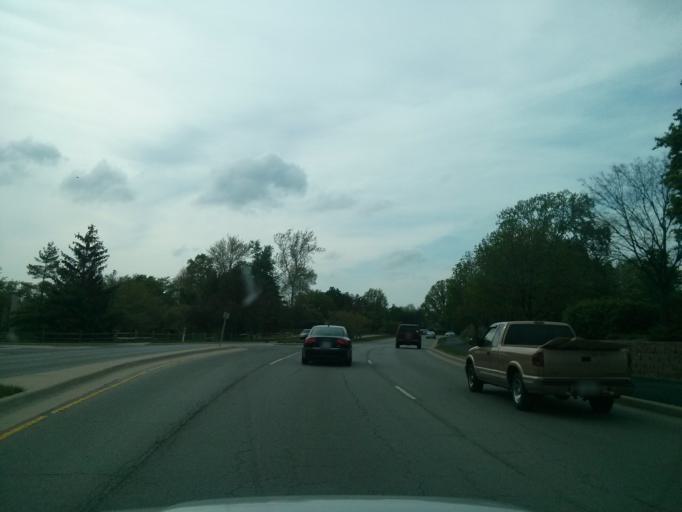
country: US
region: Indiana
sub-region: Hamilton County
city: Carmel
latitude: 39.9727
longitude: -86.1609
